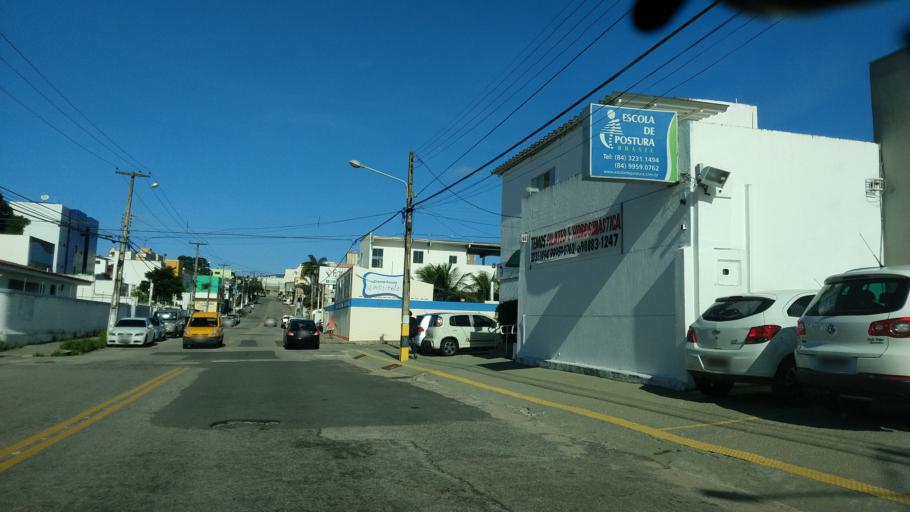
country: BR
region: Rio Grande do Norte
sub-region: Natal
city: Natal
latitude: -5.8250
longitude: -35.2057
